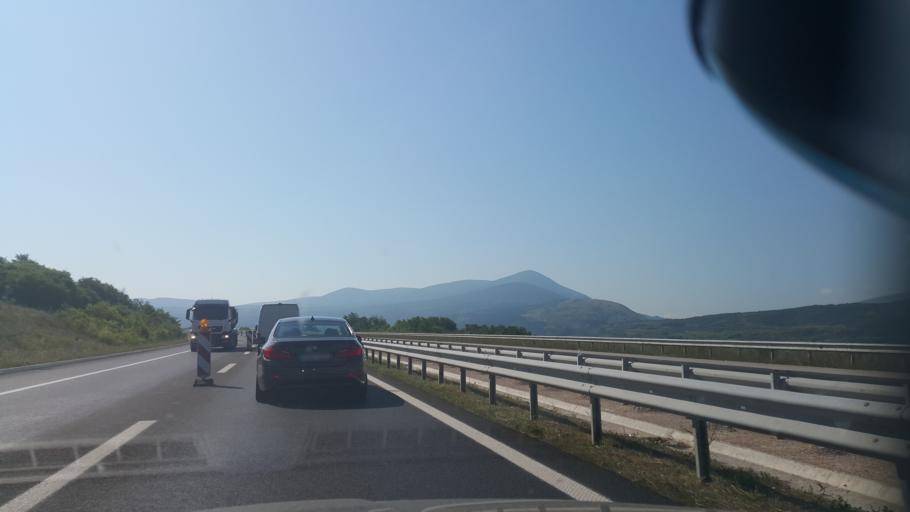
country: RS
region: Central Serbia
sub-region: Pirotski Okrug
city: Bela Palanka
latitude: 43.2406
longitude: 22.2861
